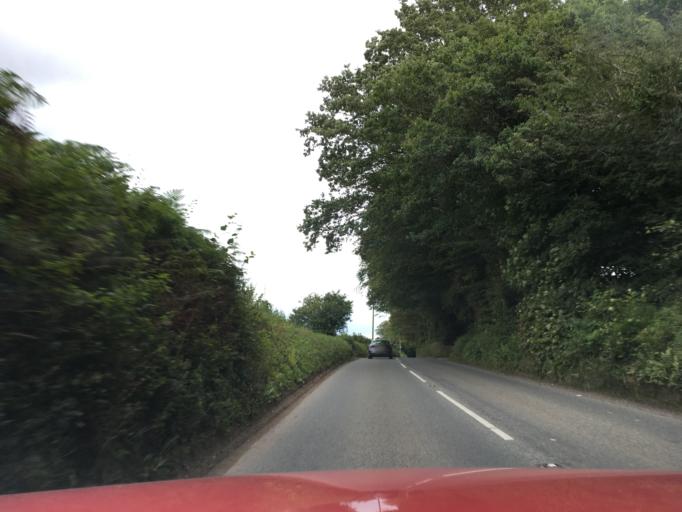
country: GB
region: England
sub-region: Devon
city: Dartmouth
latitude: 50.3559
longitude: -3.6552
